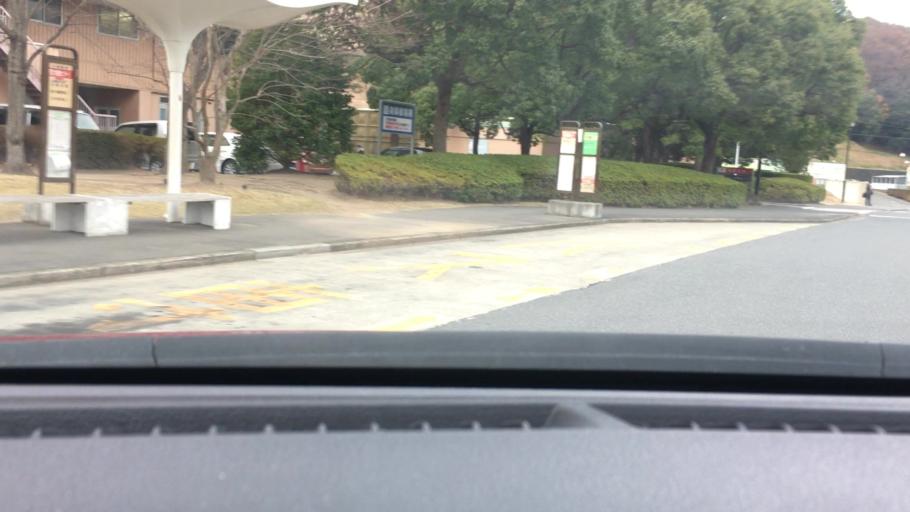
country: JP
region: Chiba
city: Ichihara
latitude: 35.4661
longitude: 140.0633
